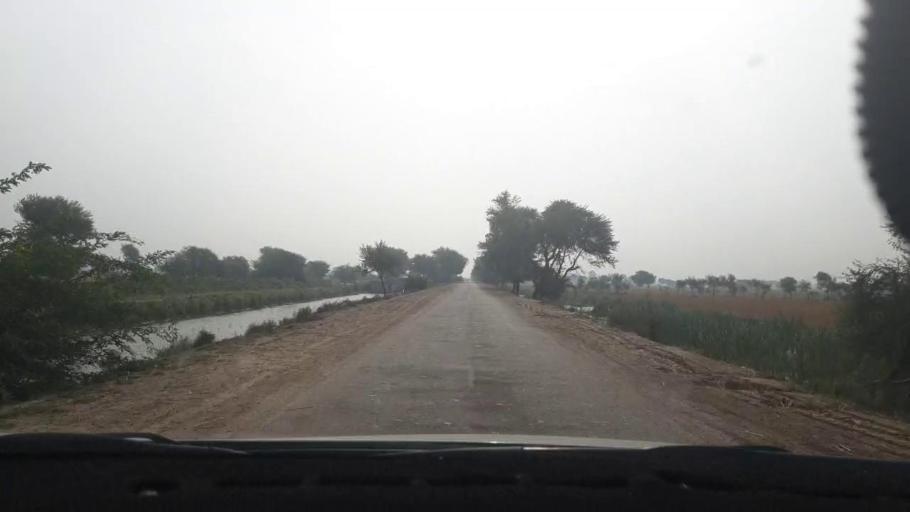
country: PK
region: Sindh
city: Tando Muhammad Khan
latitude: 25.0660
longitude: 68.5406
